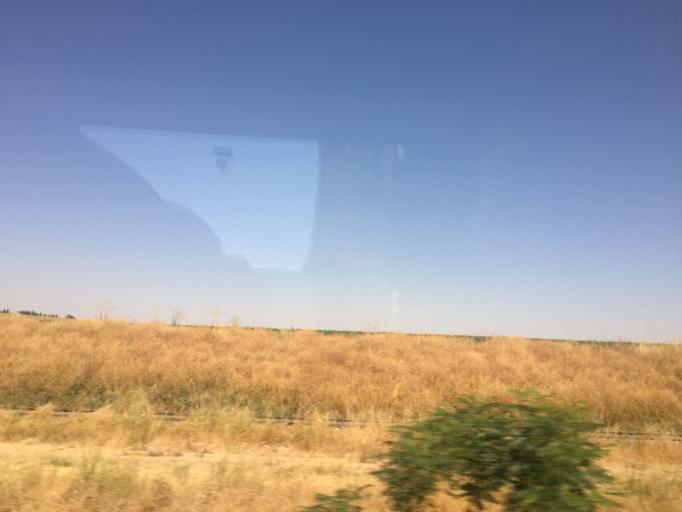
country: TR
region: Diyarbakir
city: Tepe
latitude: 37.8509
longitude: 40.7554
